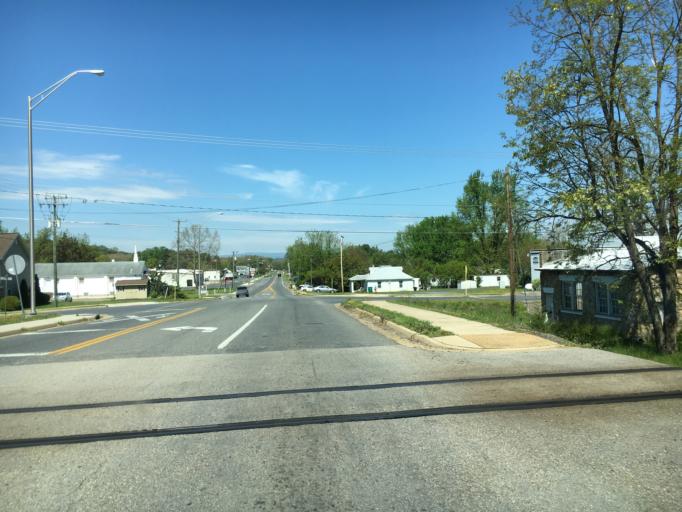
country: US
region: Virginia
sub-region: Rockingham County
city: Grottoes
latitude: 38.2610
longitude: -78.8219
